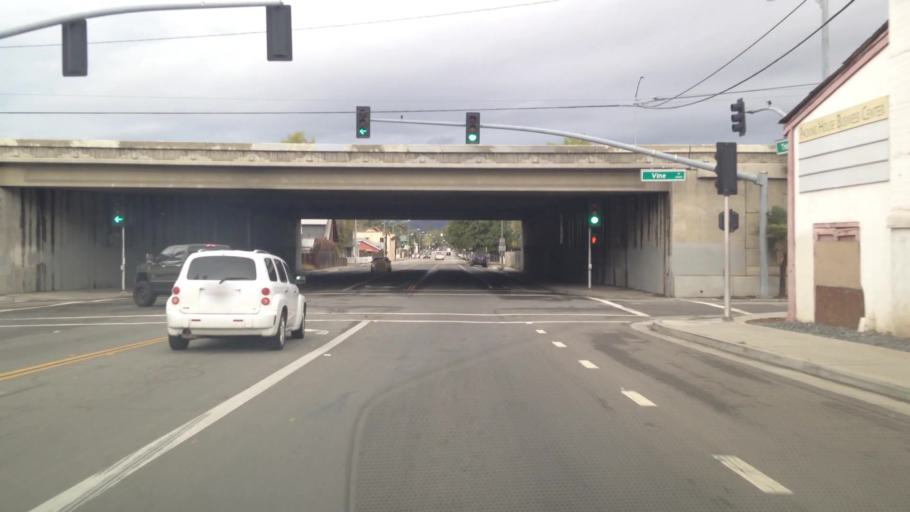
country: US
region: California
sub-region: Riverside County
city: Rubidoux
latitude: 33.9840
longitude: -117.3651
